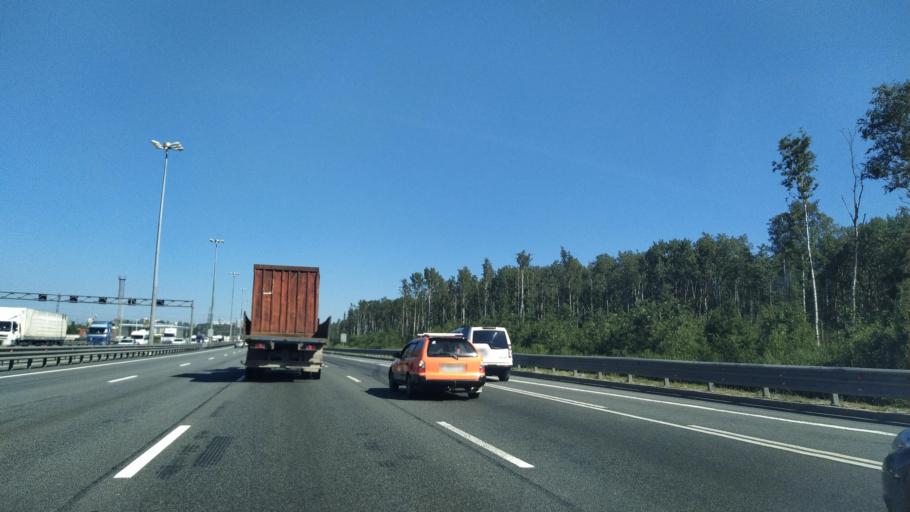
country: RU
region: Leningrad
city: Rybatskoye
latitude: 59.8743
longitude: 30.5315
